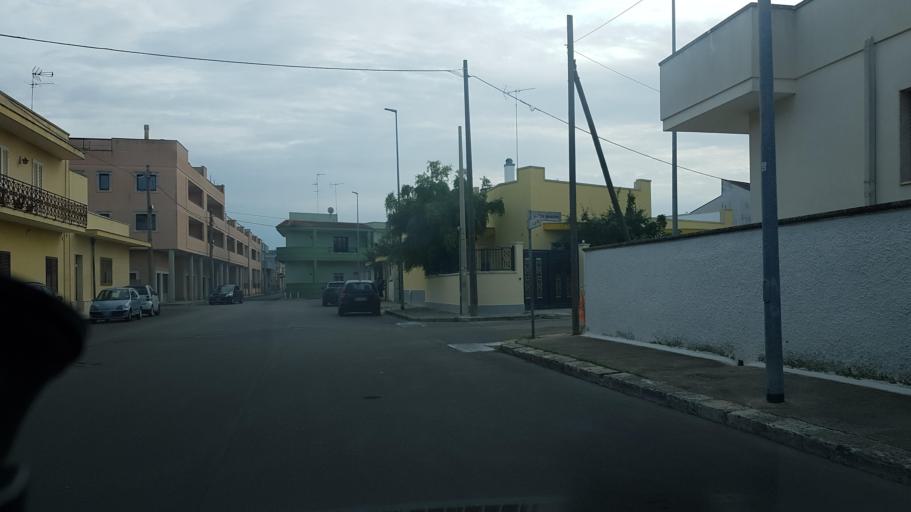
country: IT
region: Apulia
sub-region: Provincia di Lecce
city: Trepuzzi
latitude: 40.4100
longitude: 18.0705
